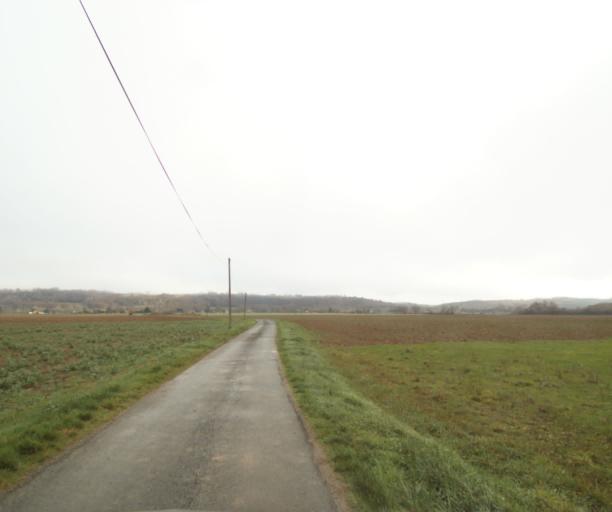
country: FR
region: Midi-Pyrenees
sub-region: Departement du Tarn-et-Garonne
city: Nohic
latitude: 43.8834
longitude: 1.4672
